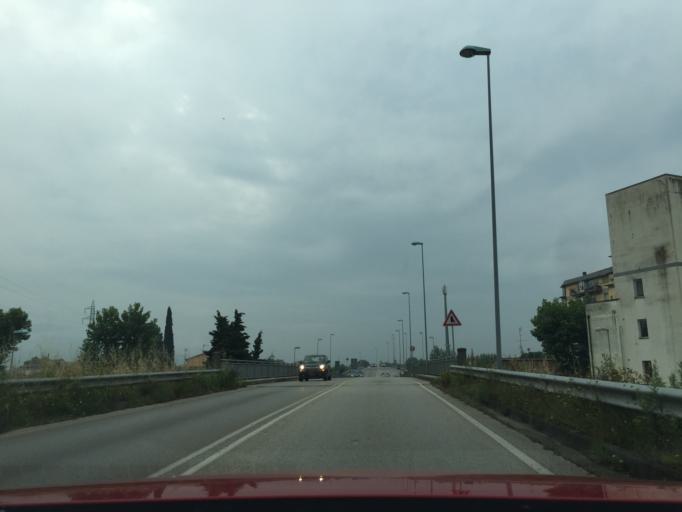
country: IT
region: Tuscany
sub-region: Provincia di Pistoia
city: Pistoia
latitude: 43.9449
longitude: 10.9000
